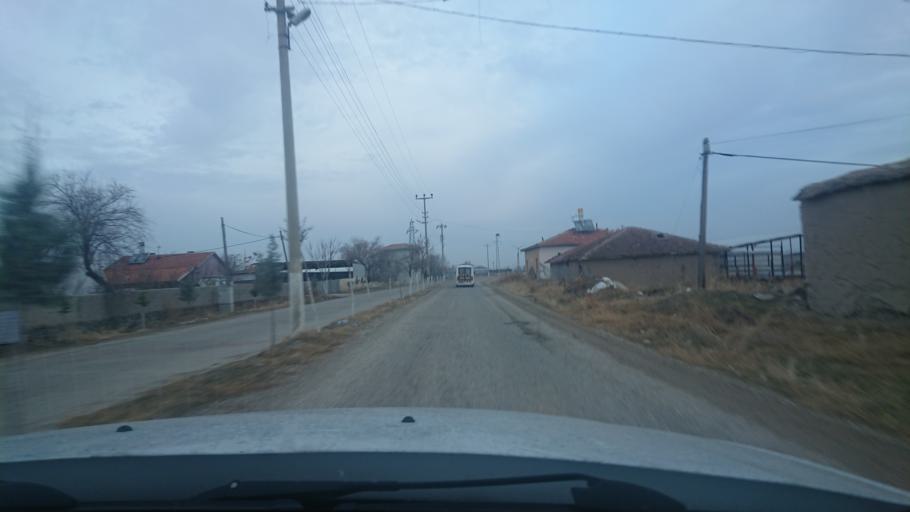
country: TR
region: Aksaray
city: Yesilova
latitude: 38.4170
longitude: 33.8361
